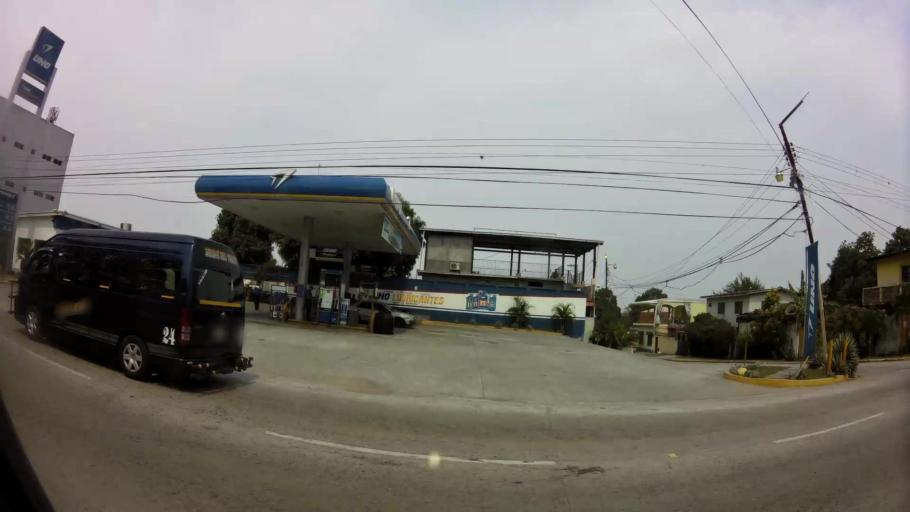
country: HN
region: Cortes
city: San Pedro Sula
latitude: 15.4905
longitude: -88.0348
